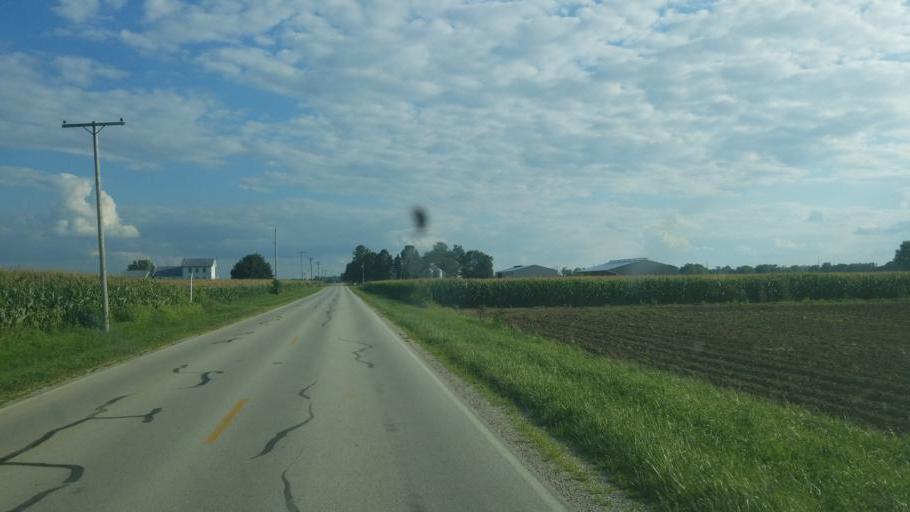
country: US
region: Ohio
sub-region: Sandusky County
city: Ballville
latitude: 41.2517
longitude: -83.1315
